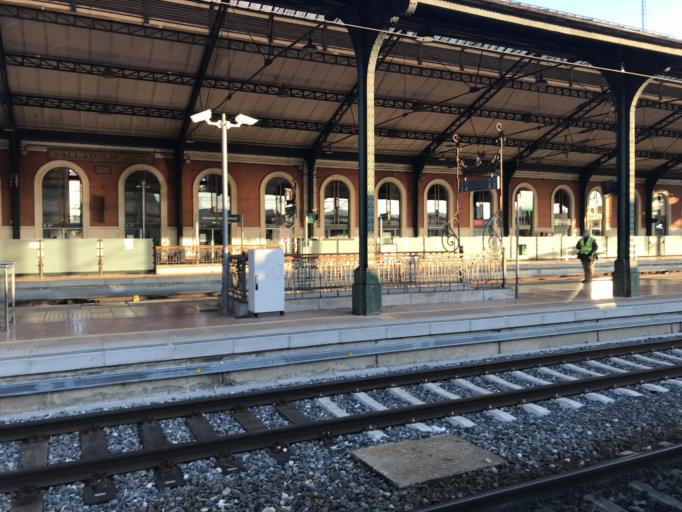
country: ES
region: Castille and Leon
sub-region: Provincia de Valladolid
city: Valladolid
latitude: 41.6419
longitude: -4.7268
